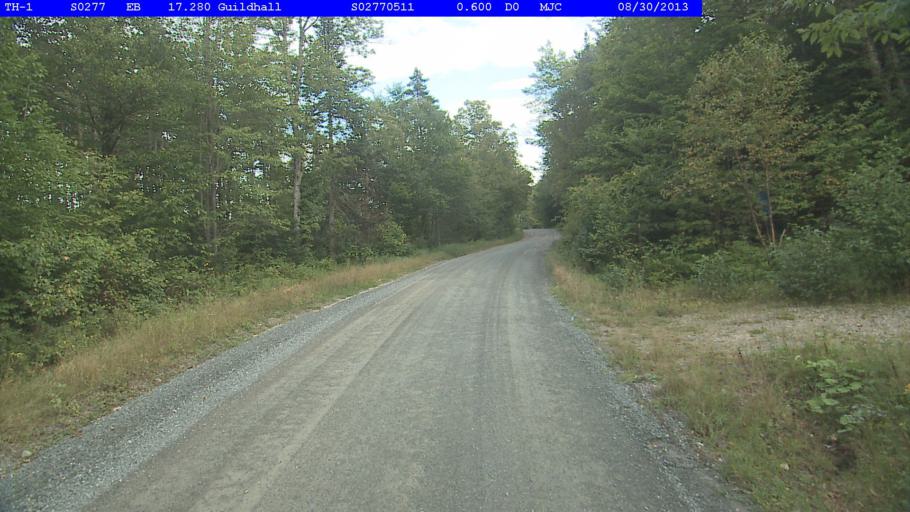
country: US
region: Vermont
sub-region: Essex County
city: Guildhall
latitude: 44.5729
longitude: -71.6578
